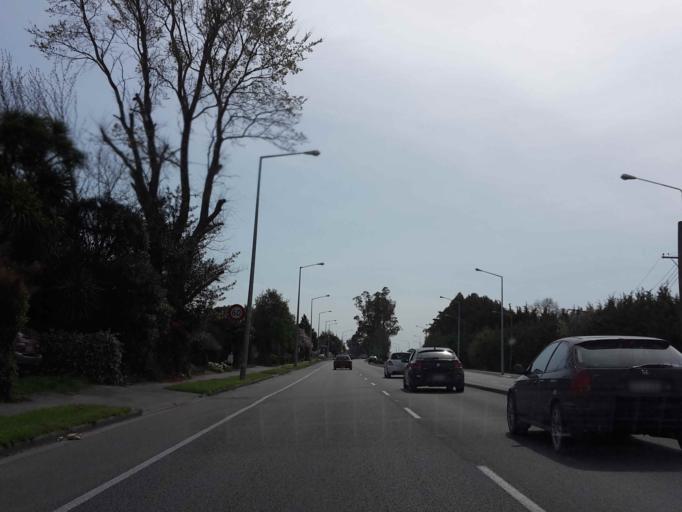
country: NZ
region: Canterbury
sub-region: Waimakariri District
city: Kaiapoi
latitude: -43.4405
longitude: 172.6354
